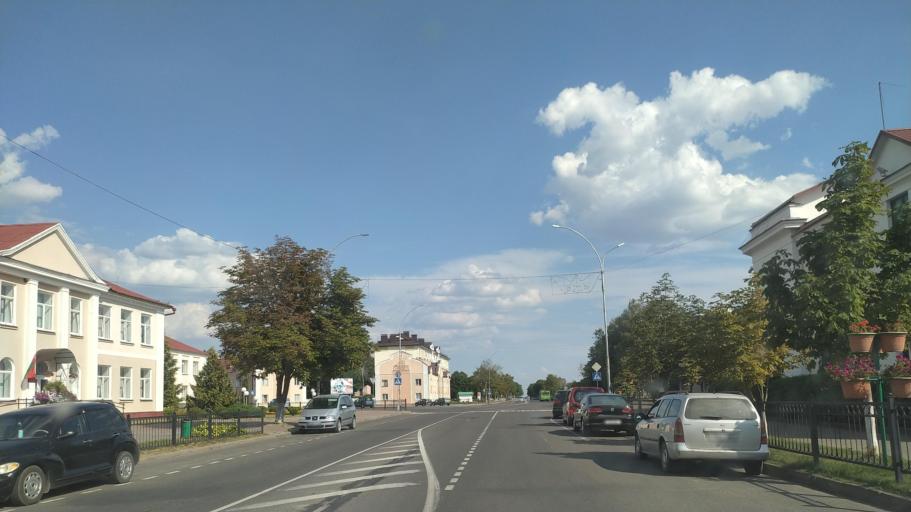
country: BY
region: Brest
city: Drahichyn
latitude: 52.1857
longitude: 25.1602
